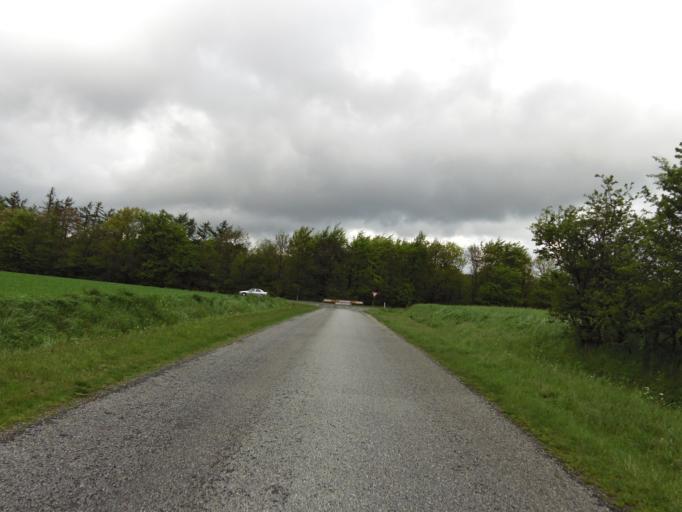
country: DK
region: South Denmark
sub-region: Haderslev Kommune
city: Gram
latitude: 55.2852
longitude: 8.9603
